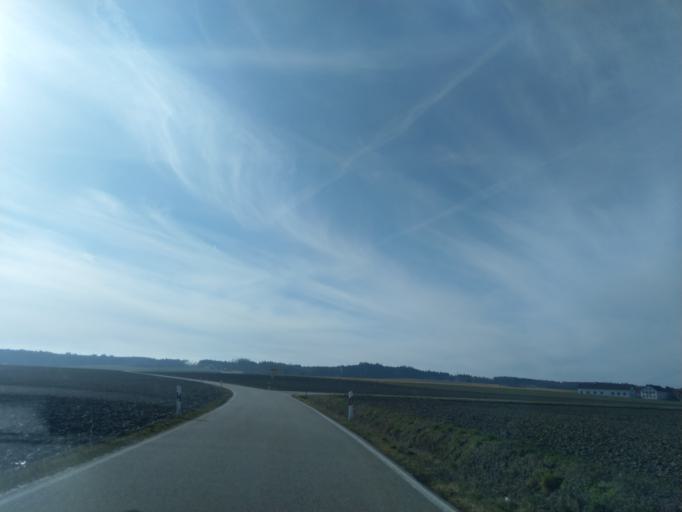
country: DE
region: Bavaria
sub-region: Lower Bavaria
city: Buchhofen
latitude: 48.6775
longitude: 12.9369
